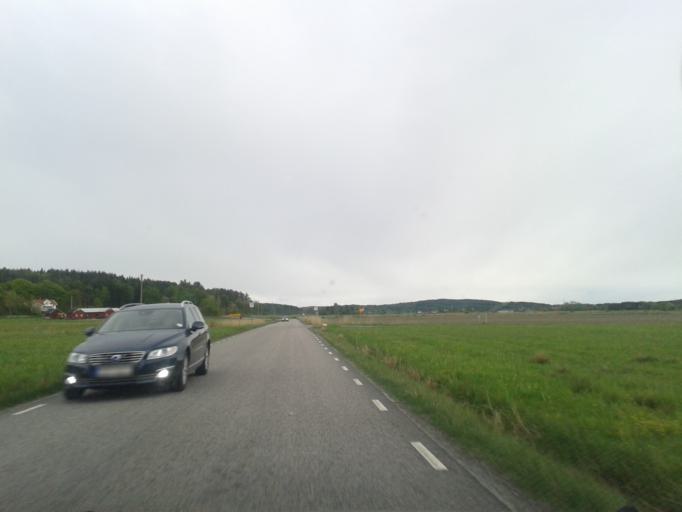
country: SE
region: Vaestra Goetaland
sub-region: Kungalvs Kommun
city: Kode
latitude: 57.9651
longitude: 11.8212
